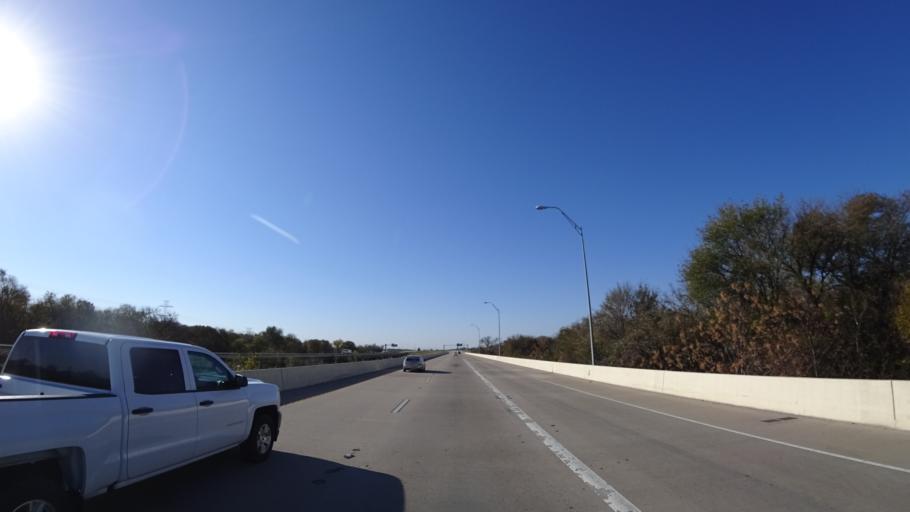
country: US
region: Texas
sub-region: Travis County
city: Manor
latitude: 30.3618
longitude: -97.5864
